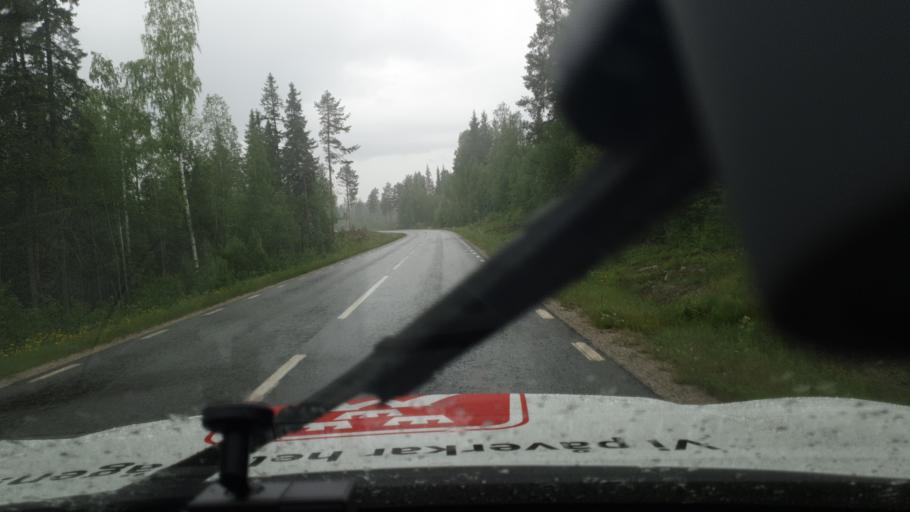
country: SE
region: Vaesterbotten
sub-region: Lycksele Kommun
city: Lycksele
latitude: 64.4454
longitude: 18.9407
